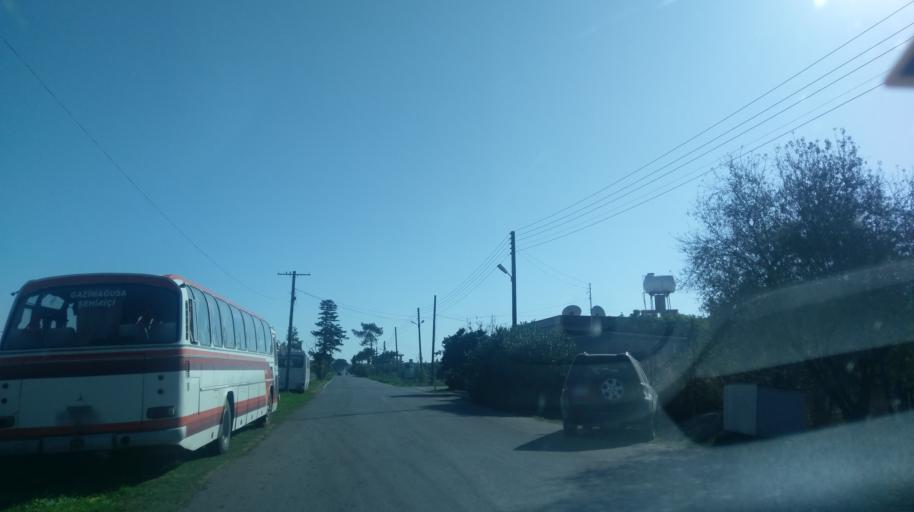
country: CY
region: Ammochostos
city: Famagusta
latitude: 35.0985
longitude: 33.9502
